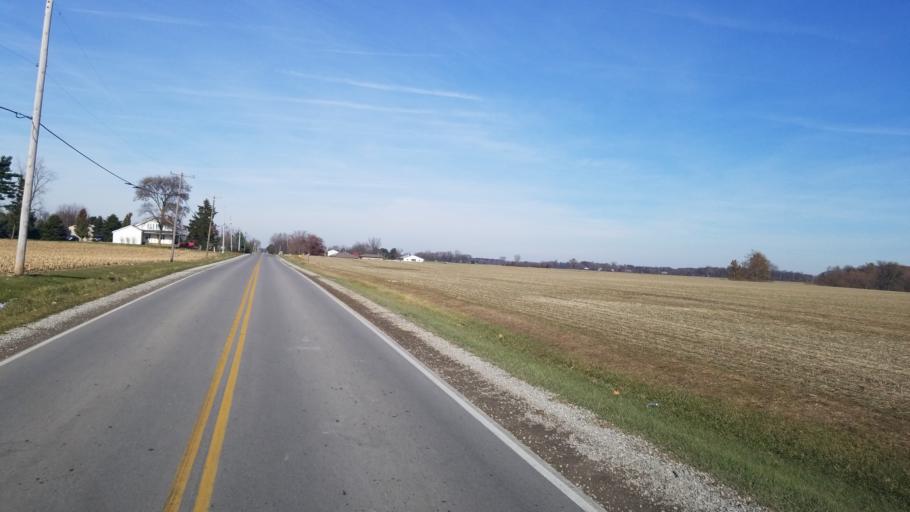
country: US
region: Ohio
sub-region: Huron County
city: Norwalk
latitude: 41.1912
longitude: -82.5899
